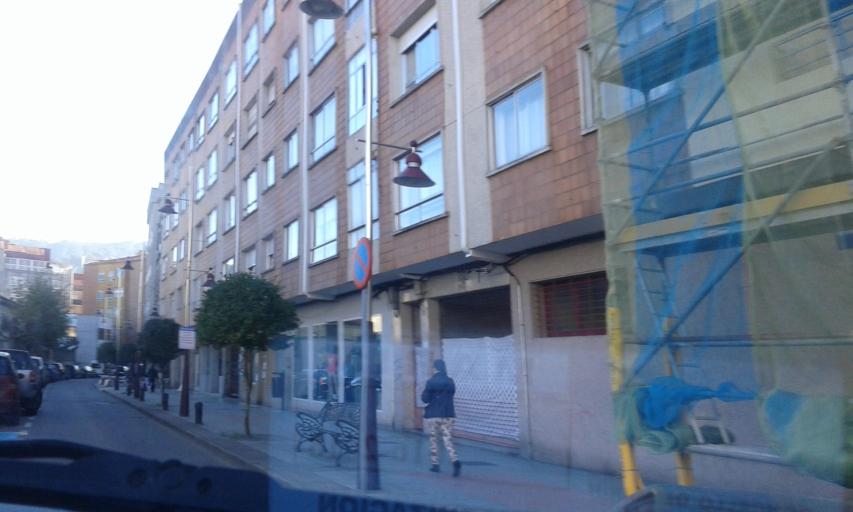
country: ES
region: Galicia
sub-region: Provincia de Pontevedra
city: Marin
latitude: 42.3926
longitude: -8.6994
